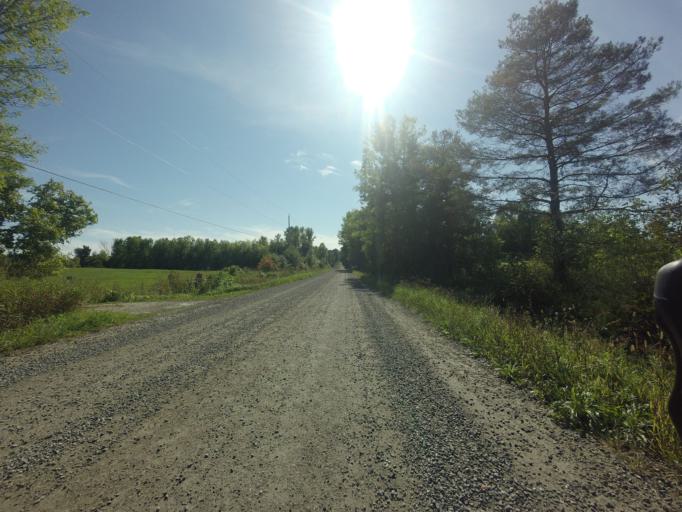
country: CA
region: Ontario
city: Perth
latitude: 44.9370
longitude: -76.3736
